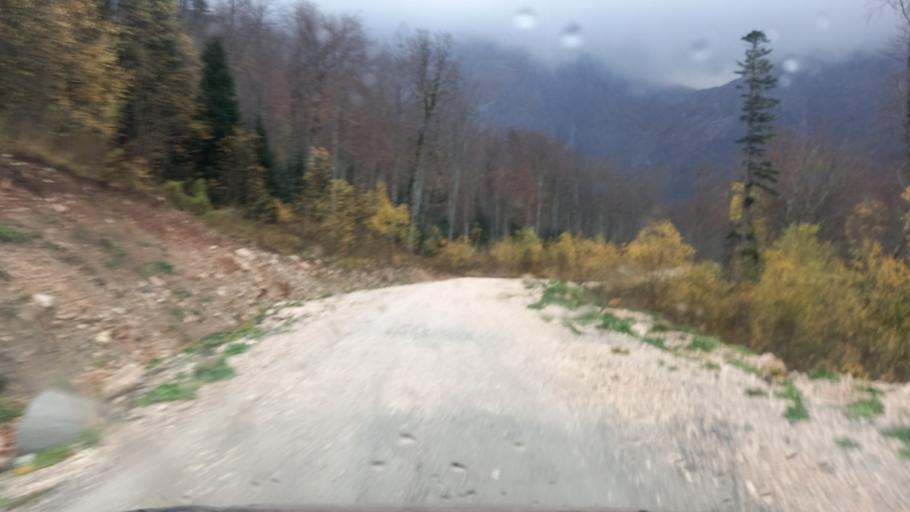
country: RU
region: Krasnodarskiy
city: Dagomys
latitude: 43.9800
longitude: 39.8586
